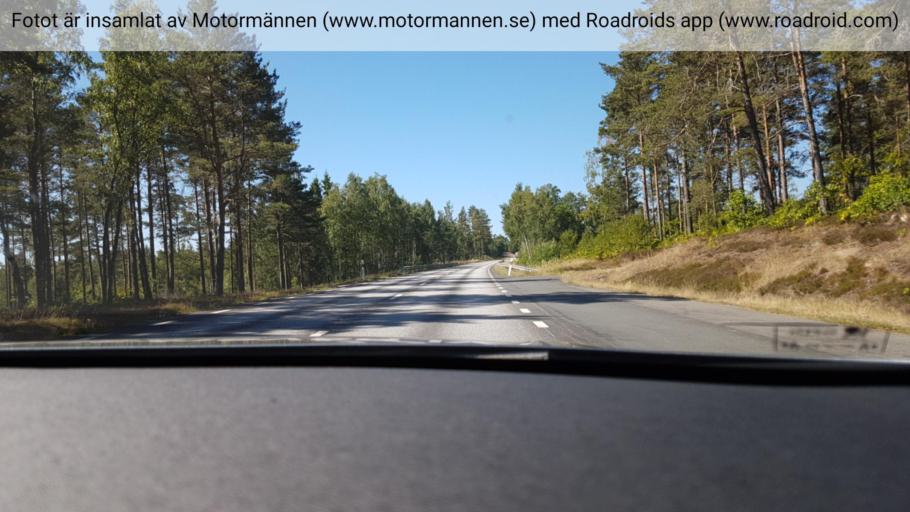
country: SE
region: Joenkoeping
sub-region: Habo Kommun
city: Habo
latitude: 58.0350
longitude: 14.1758
